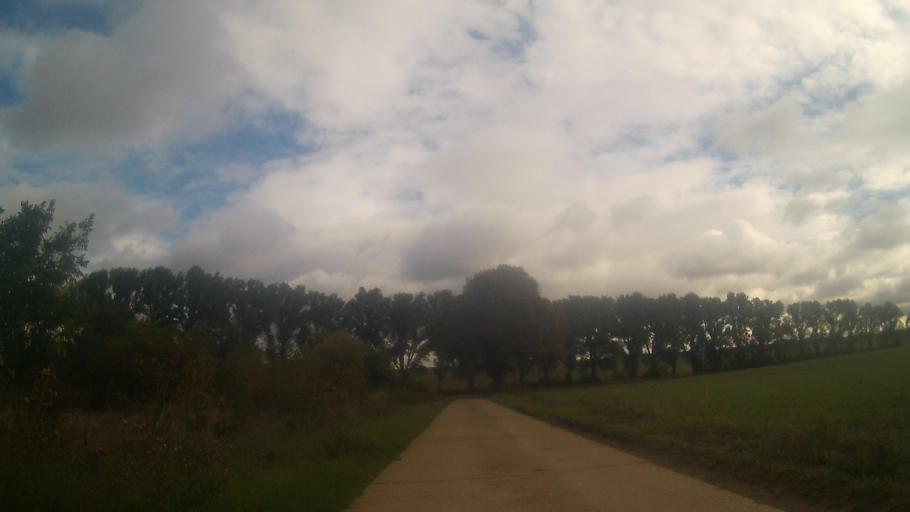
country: DE
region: Rheinland-Pfalz
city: Flonheim
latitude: 49.7903
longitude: 8.0503
